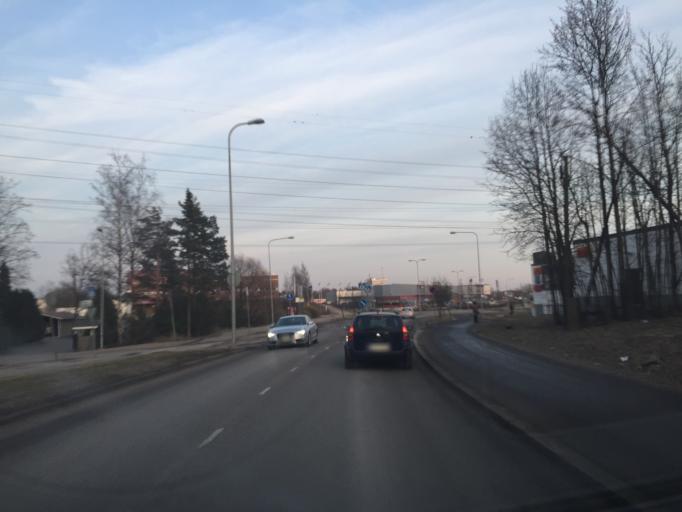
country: FI
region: Uusimaa
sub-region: Helsinki
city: Vantaa
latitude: 60.2842
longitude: 24.9685
